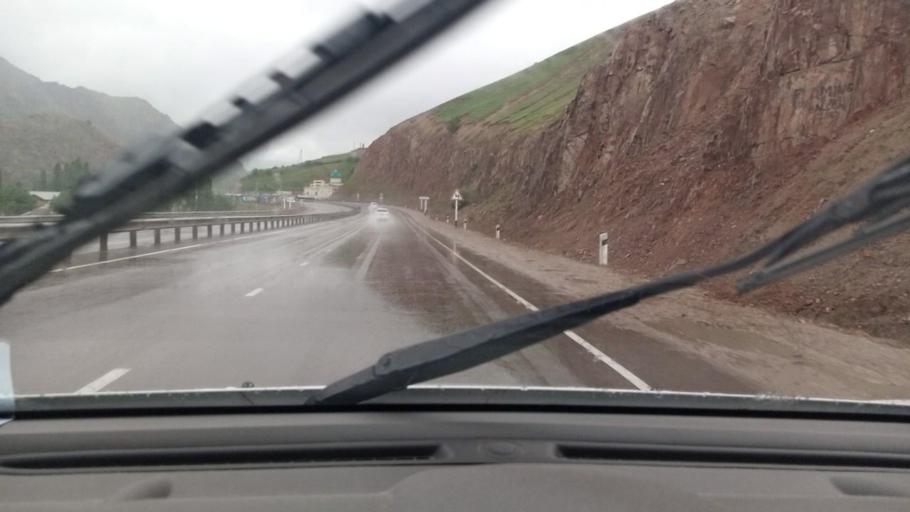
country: UZ
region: Toshkent
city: Angren
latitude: 41.1091
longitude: 70.3361
